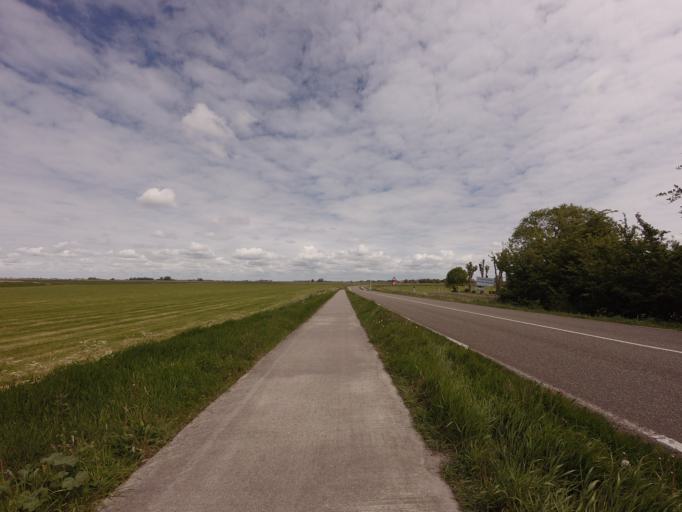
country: NL
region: Friesland
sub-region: Sudwest Fryslan
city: Koudum
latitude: 52.8922
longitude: 5.4915
